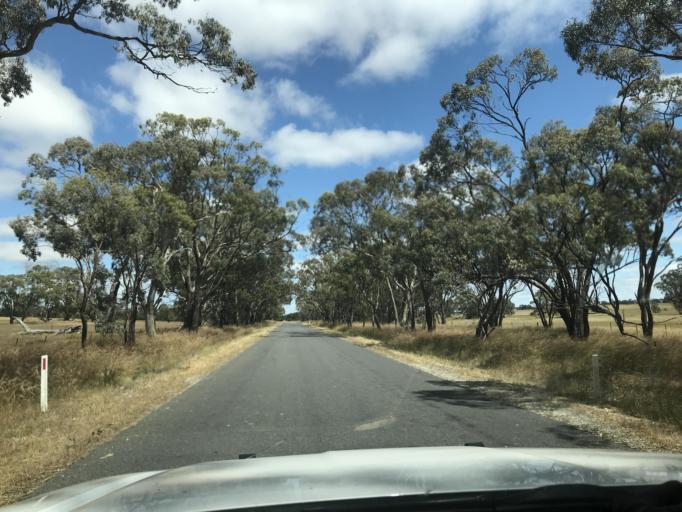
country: AU
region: South Australia
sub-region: Tatiara
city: Bordertown
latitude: -36.3107
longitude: 141.0273
